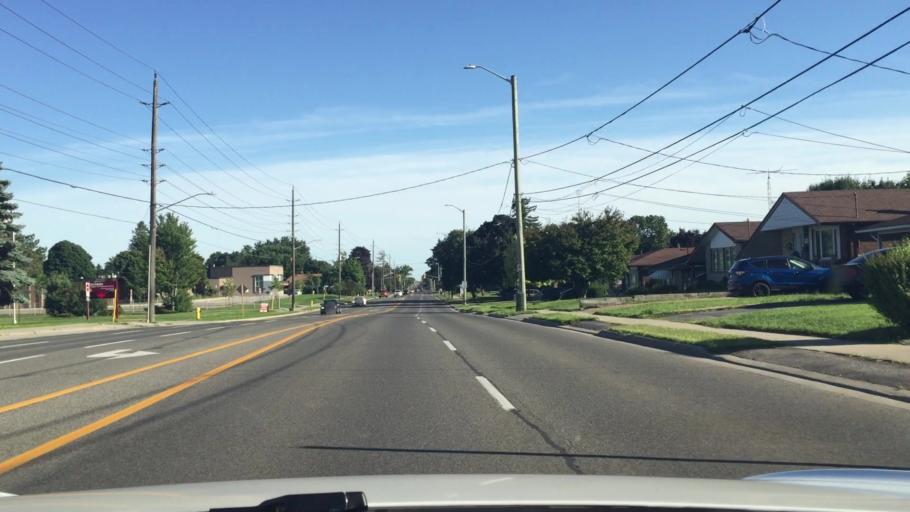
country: CA
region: Ontario
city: Oshawa
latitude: 43.9119
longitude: -78.8375
